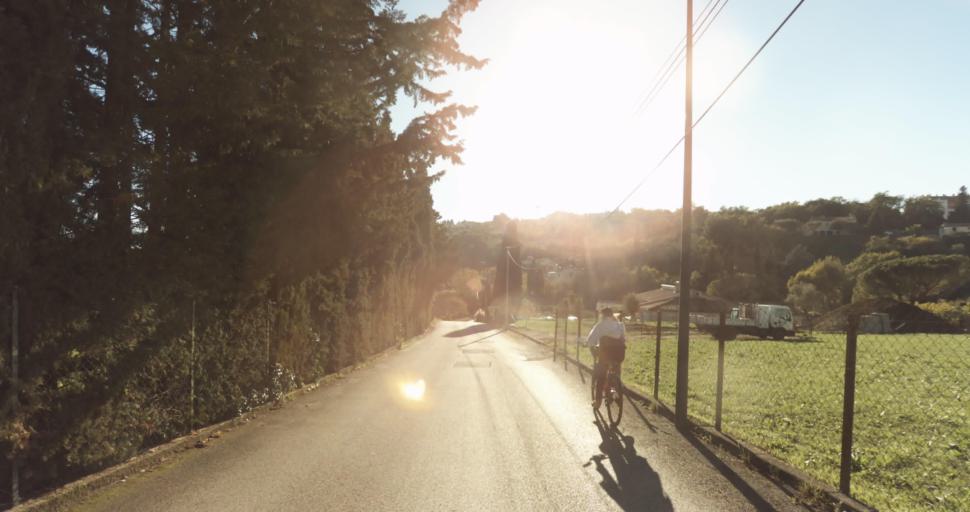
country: FR
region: Provence-Alpes-Cote d'Azur
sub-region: Departement des Alpes-Maritimes
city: Vence
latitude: 43.7266
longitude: 7.1268
